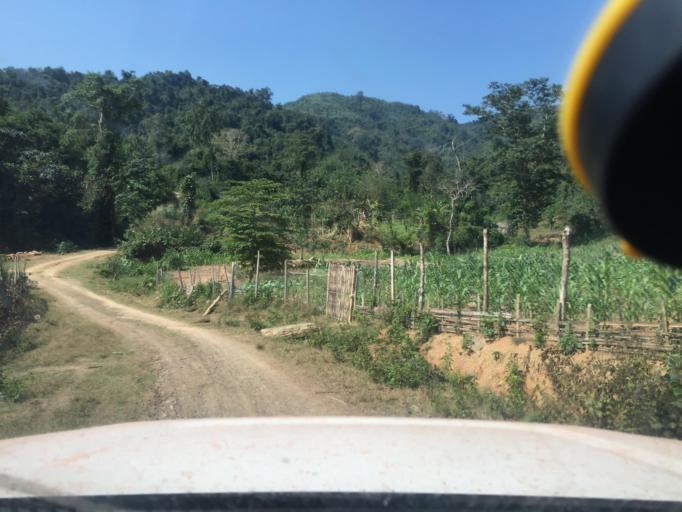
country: LA
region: Phongsali
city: Phongsali
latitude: 21.6588
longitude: 102.4205
